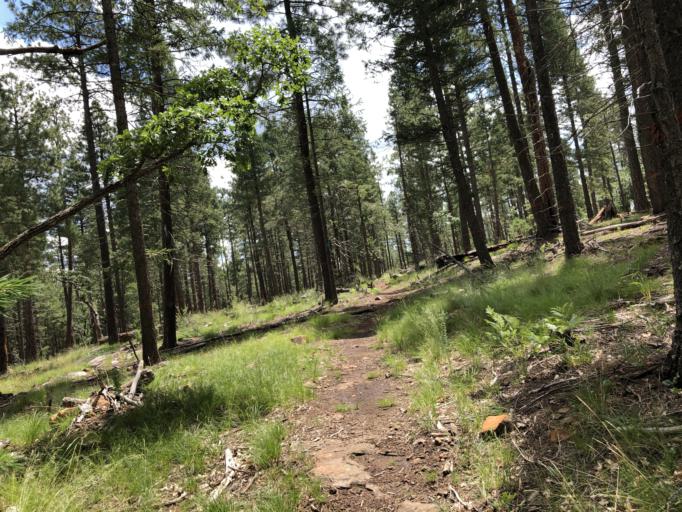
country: US
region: Arizona
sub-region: Gila County
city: Star Valley
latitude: 34.3353
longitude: -110.9494
